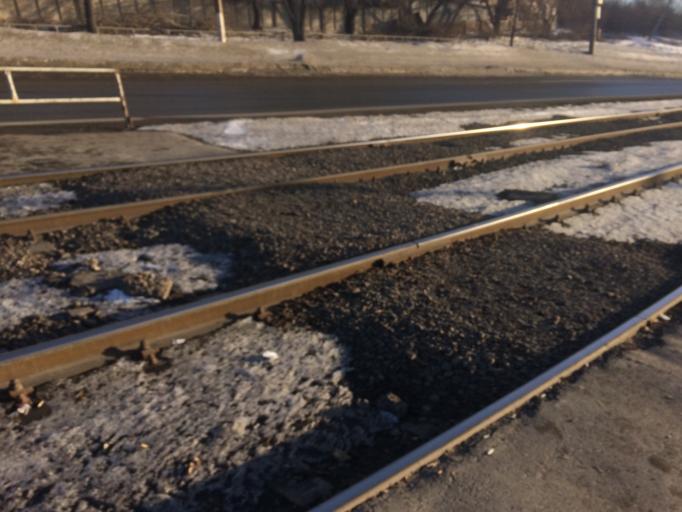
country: RU
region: Chelyabinsk
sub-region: Gorod Magnitogorsk
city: Magnitogorsk
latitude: 53.3955
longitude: 59.0279
